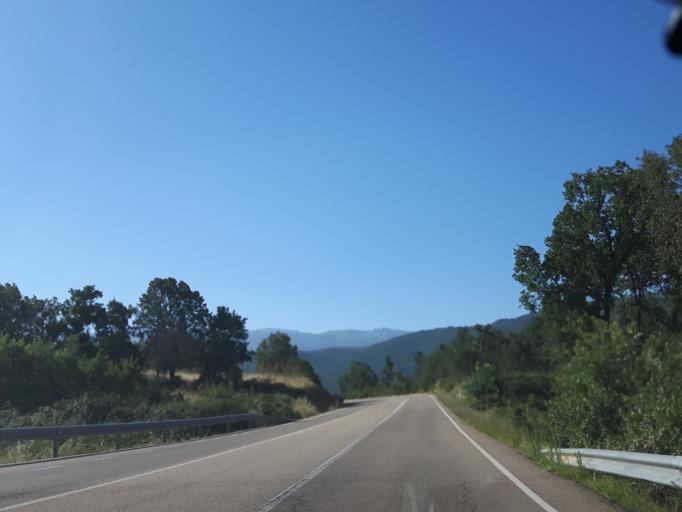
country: ES
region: Castille and Leon
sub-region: Provincia de Salamanca
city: Navalmoral de Bejar
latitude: 40.4044
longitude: -5.7947
